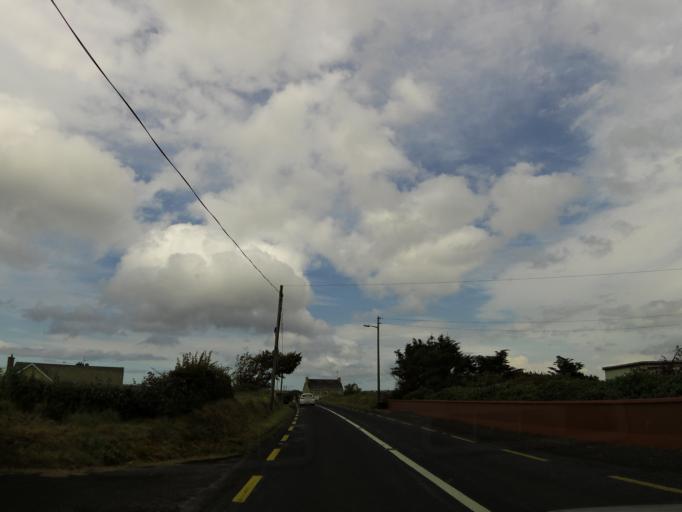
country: IE
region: Munster
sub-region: An Clar
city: Kilrush
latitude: 52.7154
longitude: -9.5893
